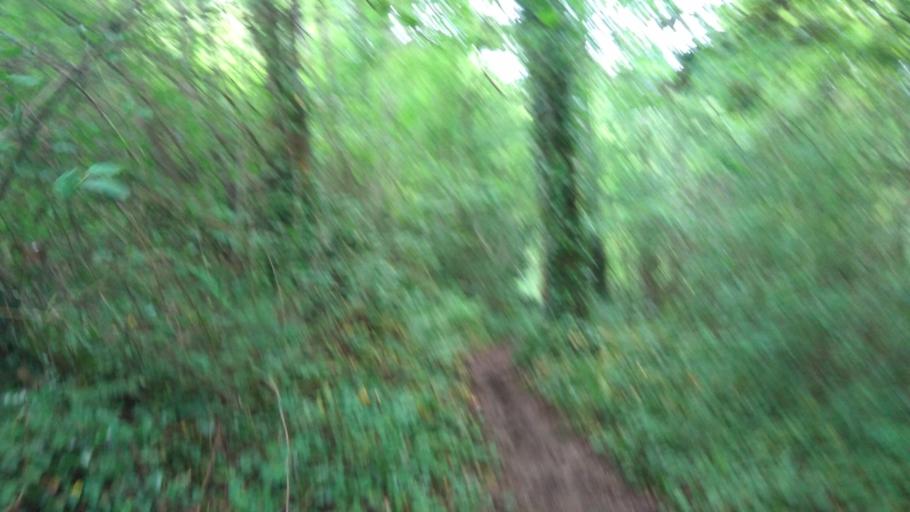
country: FR
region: Aquitaine
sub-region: Departement des Pyrenees-Atlantiques
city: Mazeres-Lezons
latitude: 43.2725
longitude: -0.3542
